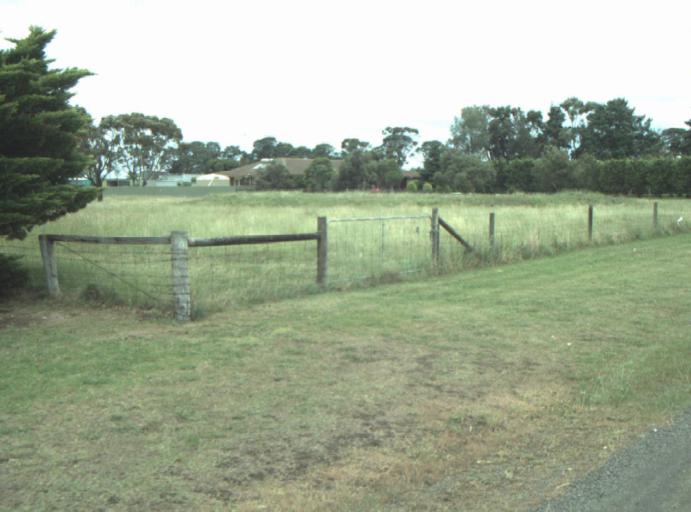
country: AU
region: Victoria
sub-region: Greater Geelong
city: Leopold
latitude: -38.2077
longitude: 144.4513
